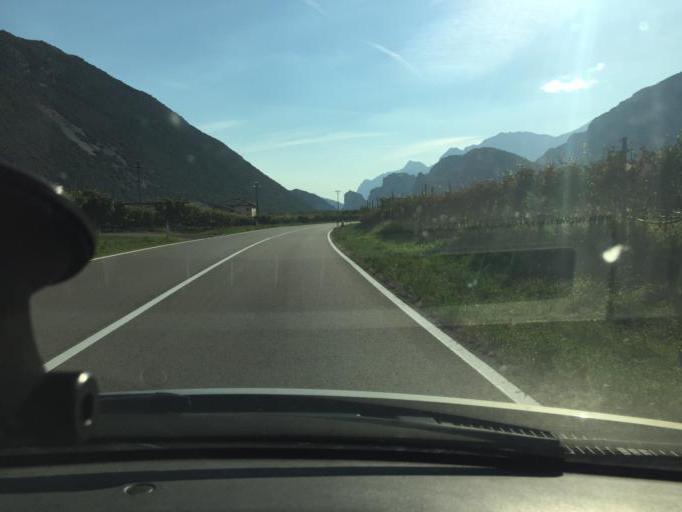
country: IT
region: Trentino-Alto Adige
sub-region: Provincia di Trento
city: Dro
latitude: 45.9665
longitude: 10.9221
